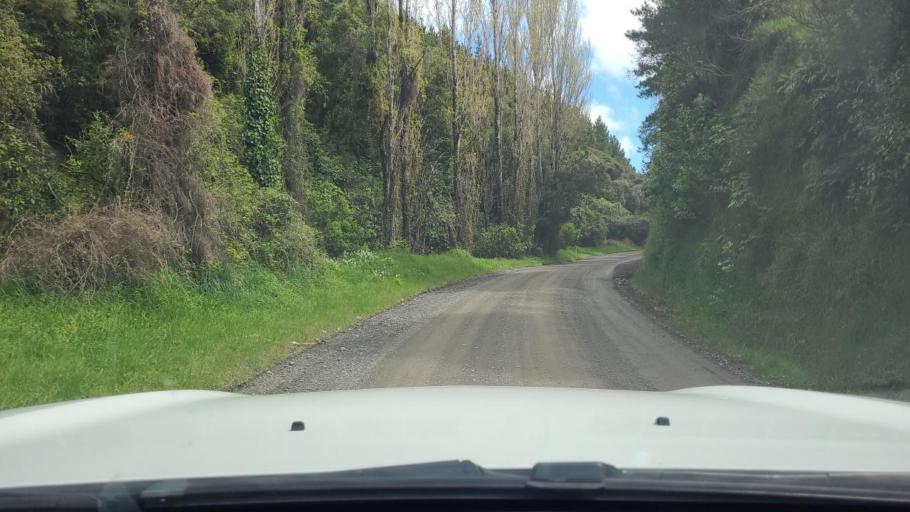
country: NZ
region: Wellington
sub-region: South Wairarapa District
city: Waipawa
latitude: -41.3228
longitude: 175.4225
